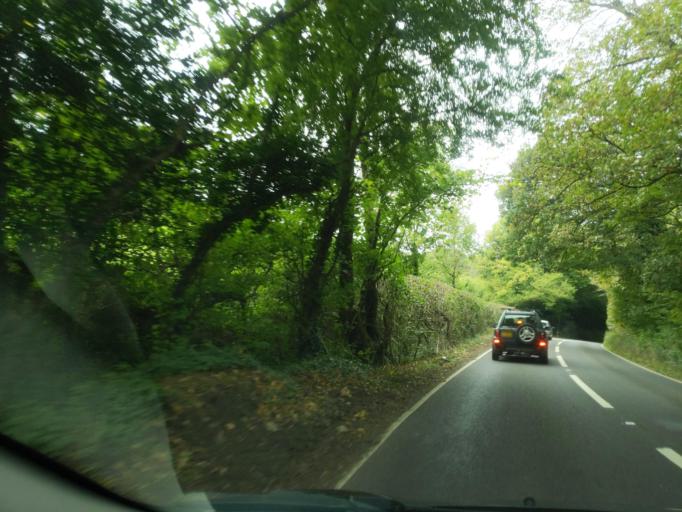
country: GB
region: England
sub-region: Cornwall
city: Wadebridge
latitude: 50.5049
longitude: -4.7799
